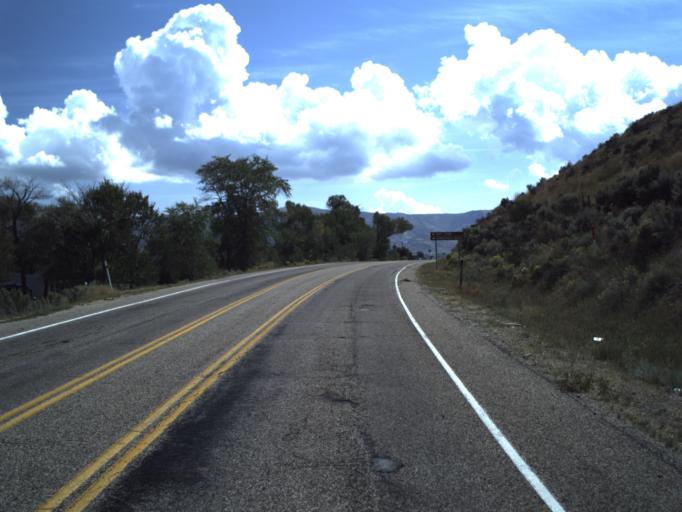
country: US
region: Utah
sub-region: Rich County
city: Randolph
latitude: 41.8482
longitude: -111.3534
